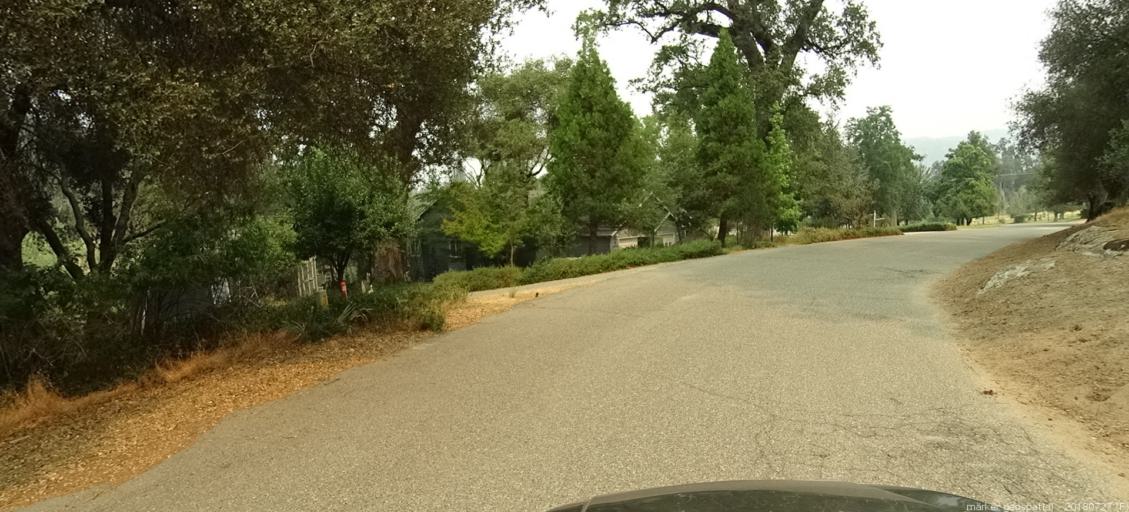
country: US
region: California
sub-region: Madera County
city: Oakhurst
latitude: 37.3212
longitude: -119.6267
